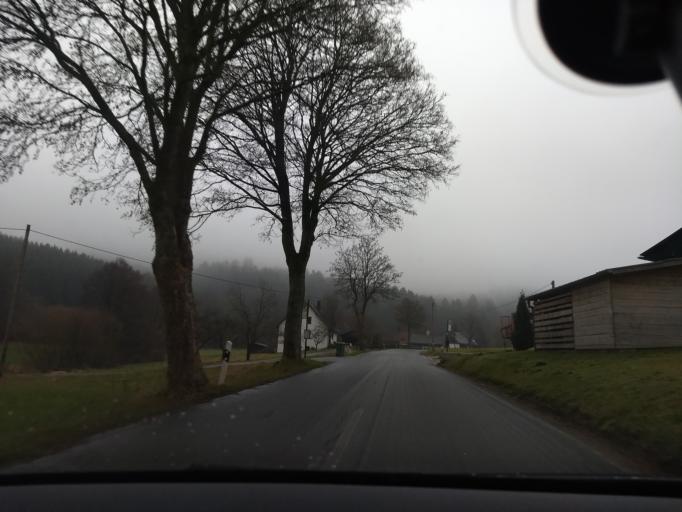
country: DE
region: North Rhine-Westphalia
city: Eslohe
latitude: 51.2528
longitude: 8.1466
